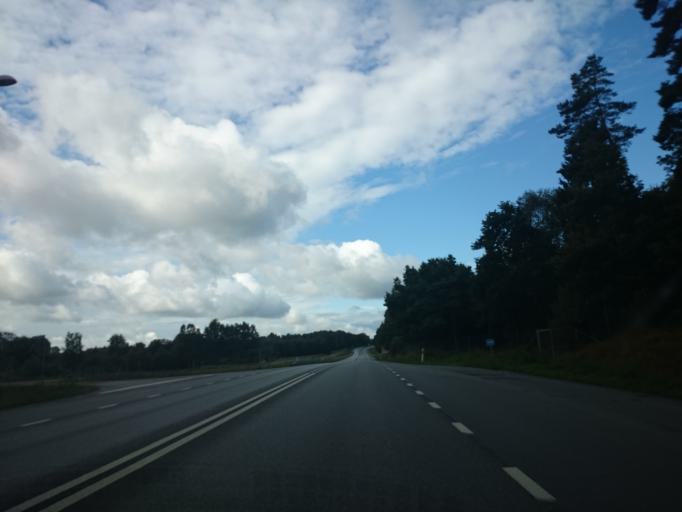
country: SE
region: Skane
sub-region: Horby Kommun
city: Hoerby
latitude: 55.9250
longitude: 13.7936
